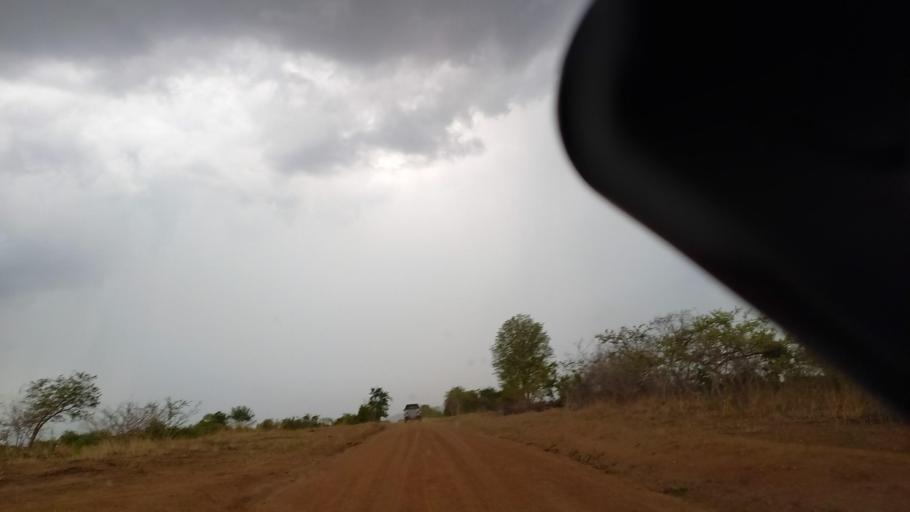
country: ZM
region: Lusaka
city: Kafue
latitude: -15.8677
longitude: 28.1914
